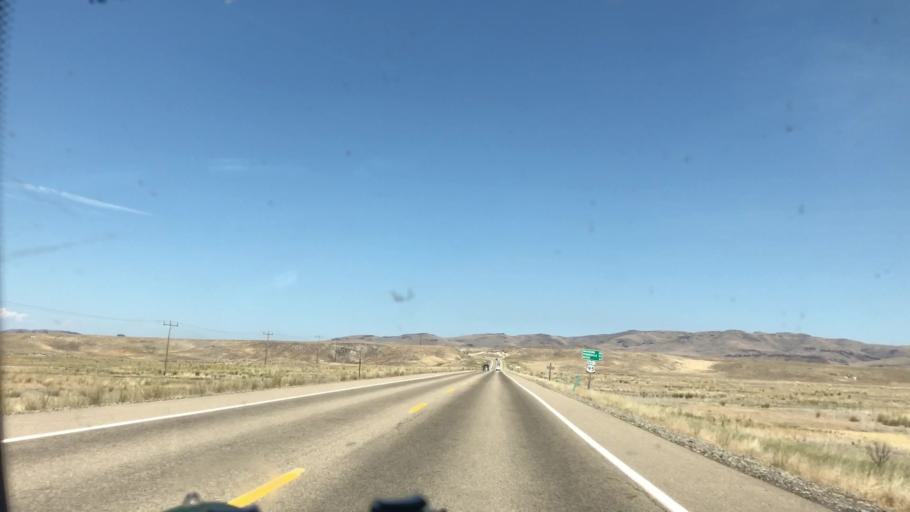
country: US
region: Idaho
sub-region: Owyhee County
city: Marsing
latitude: 43.2558
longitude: -117.0179
